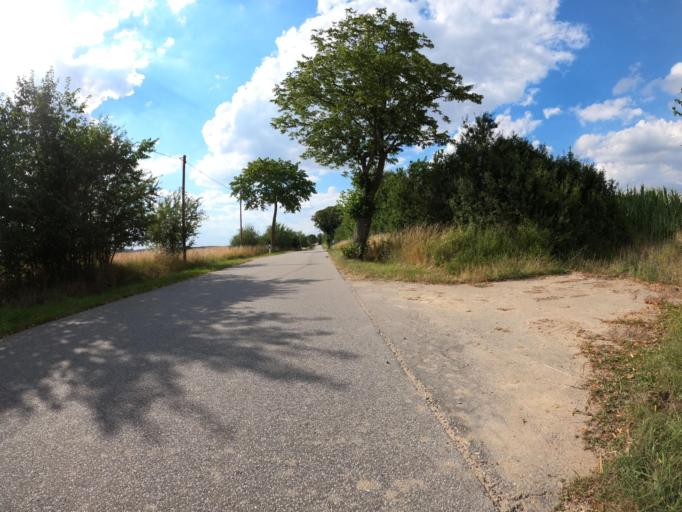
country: DE
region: Mecklenburg-Vorpommern
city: Woldegk
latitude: 53.4429
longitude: 13.5896
